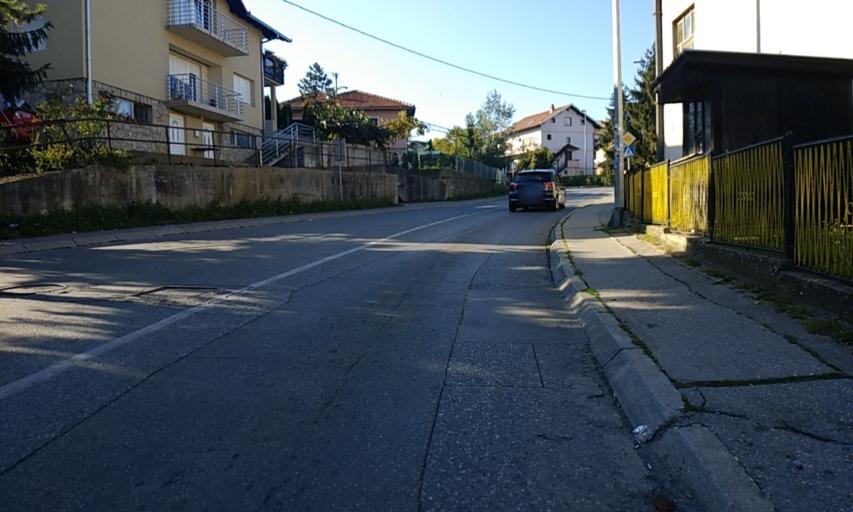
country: BA
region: Republika Srpska
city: Banja Luka
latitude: 44.7786
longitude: 17.1847
